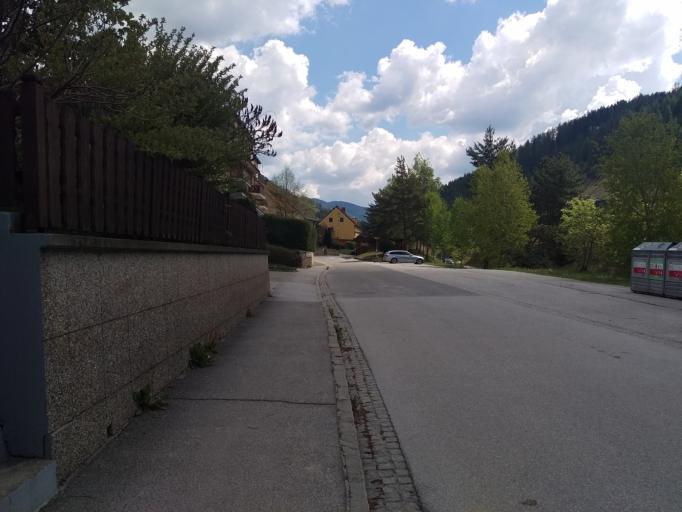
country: AT
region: Styria
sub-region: Politischer Bezirk Bruck-Muerzzuschlag
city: Allerheiligen im Muerztal
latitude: 47.3909
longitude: 15.4328
